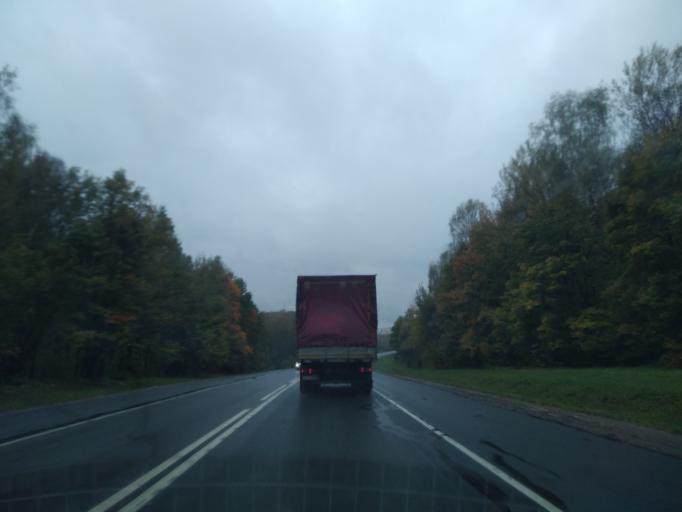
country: RU
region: Tula
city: Barsuki
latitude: 54.3219
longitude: 37.5520
